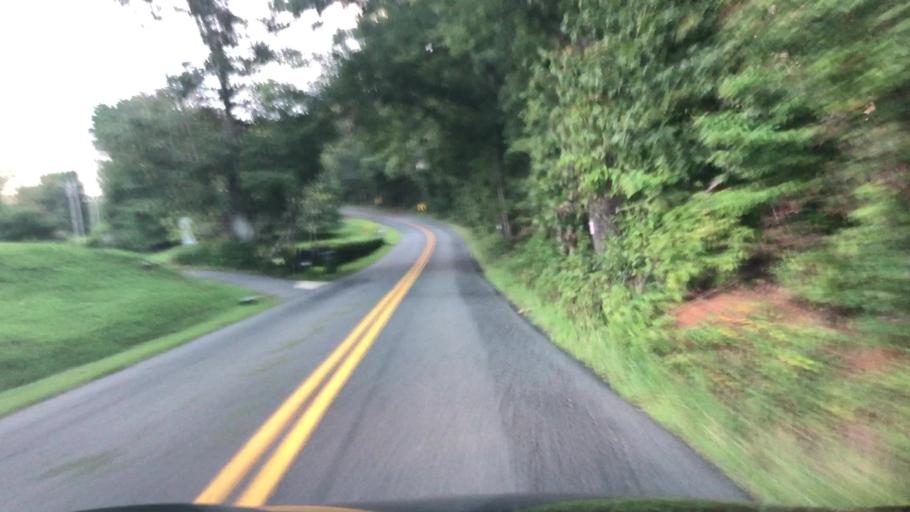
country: US
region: Virginia
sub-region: Stafford County
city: Stafford
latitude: 38.4796
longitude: -77.5796
